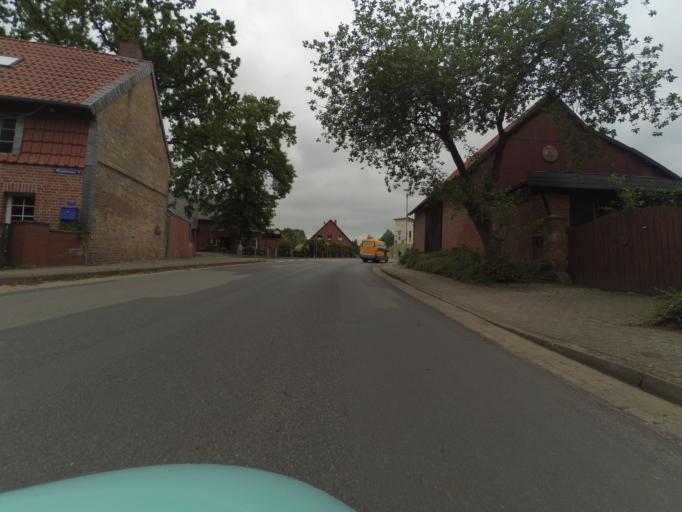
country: DE
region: Lower Saxony
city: Didderse
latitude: 52.3816
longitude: 10.4032
